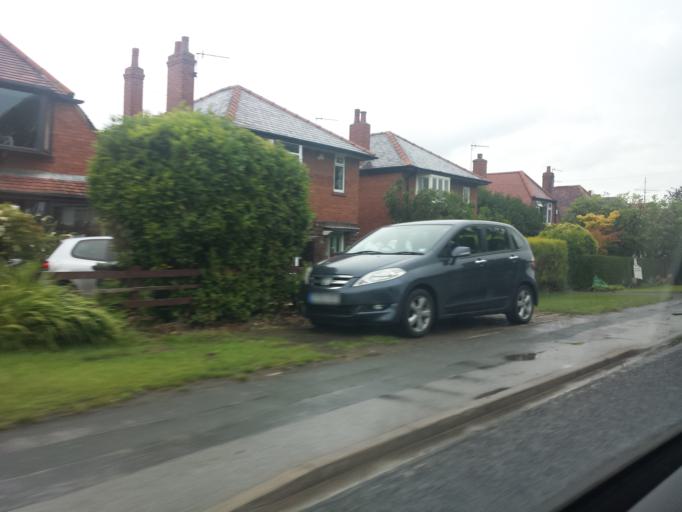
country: GB
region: England
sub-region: Bradford
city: Ilkley
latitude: 53.9290
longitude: -1.8067
